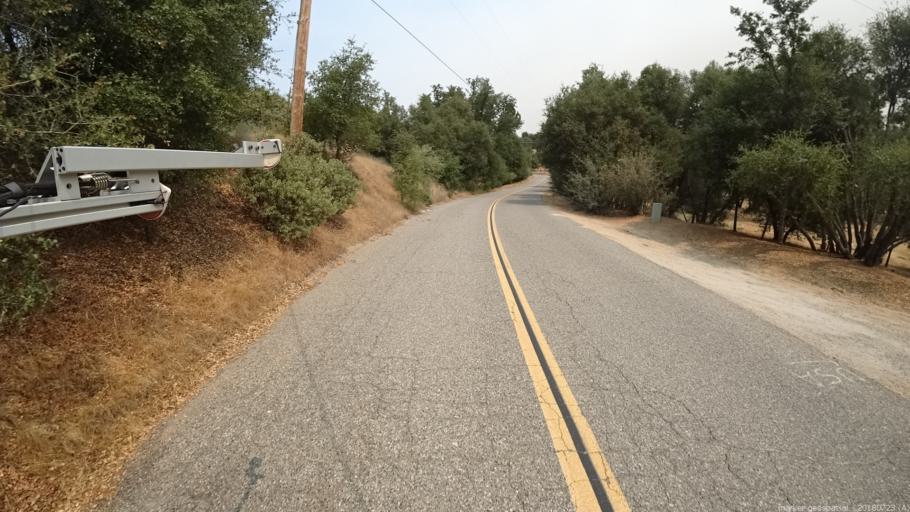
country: US
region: California
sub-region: Madera County
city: Ahwahnee
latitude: 37.3404
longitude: -119.7037
